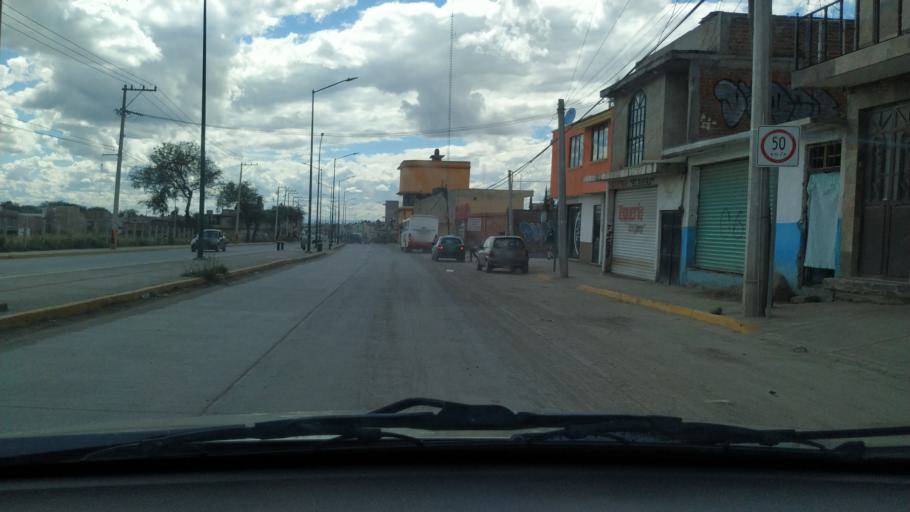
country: MX
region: Guanajuato
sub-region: Leon
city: Medina
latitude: 21.1519
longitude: -101.6273
